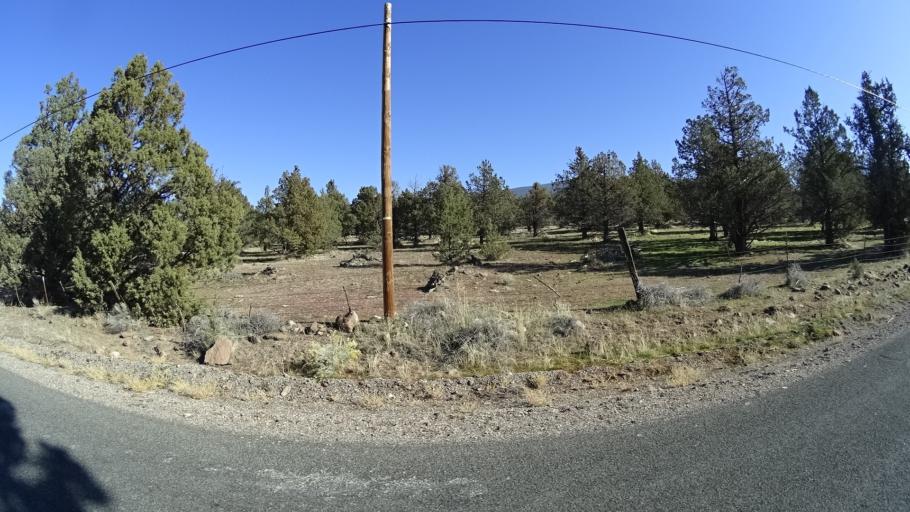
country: US
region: California
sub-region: Siskiyou County
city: Weed
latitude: 41.6318
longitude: -122.3353
